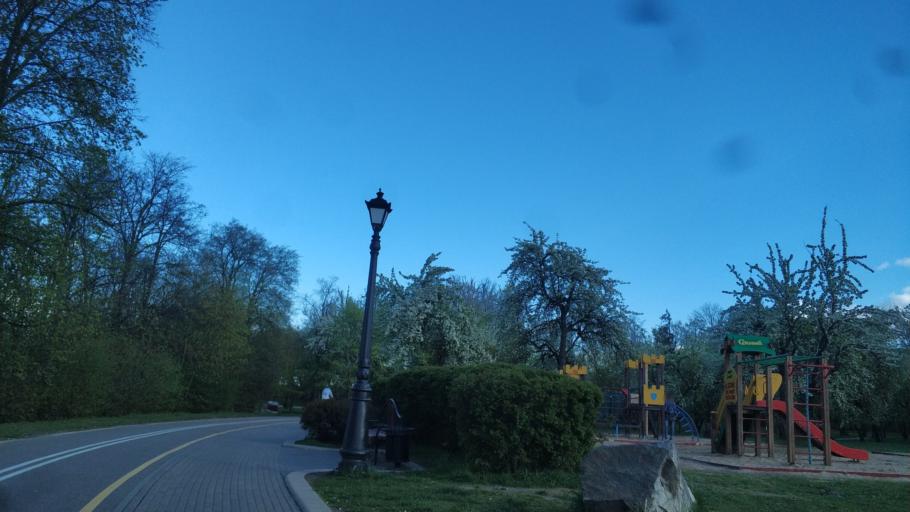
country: BY
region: Minsk
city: Minsk
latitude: 53.8561
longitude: 27.5797
